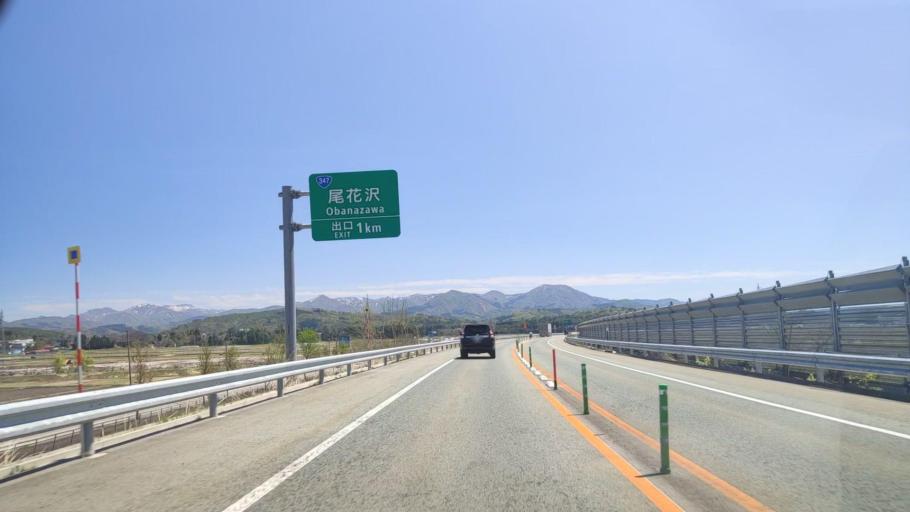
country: JP
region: Yamagata
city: Obanazawa
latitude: 38.6154
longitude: 140.3867
